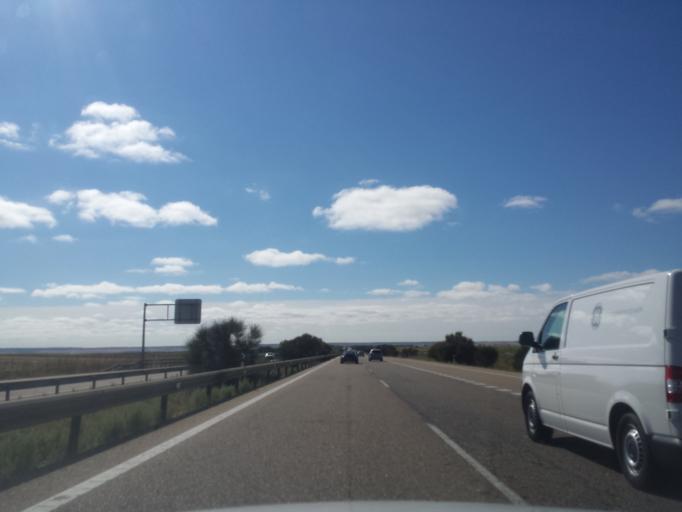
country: ES
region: Castille and Leon
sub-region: Provincia de Valladolid
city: San Pedro de Latarce
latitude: 41.7982
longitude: -5.3415
